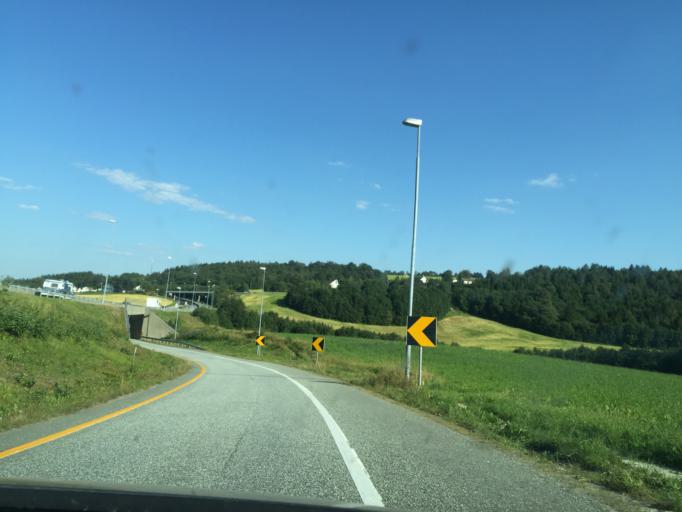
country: NO
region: Sor-Trondelag
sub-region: Malvik
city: Malvik
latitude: 63.4255
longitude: 10.6898
